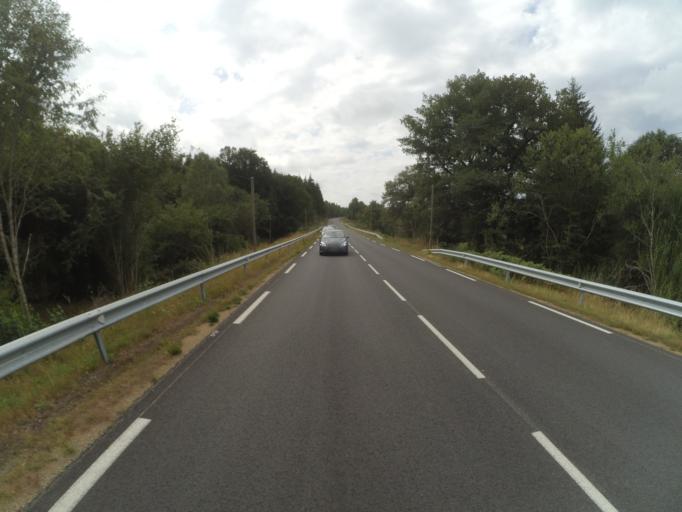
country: FR
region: Limousin
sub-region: Departement de la Creuse
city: La Courtine
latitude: 45.6327
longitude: 2.2771
